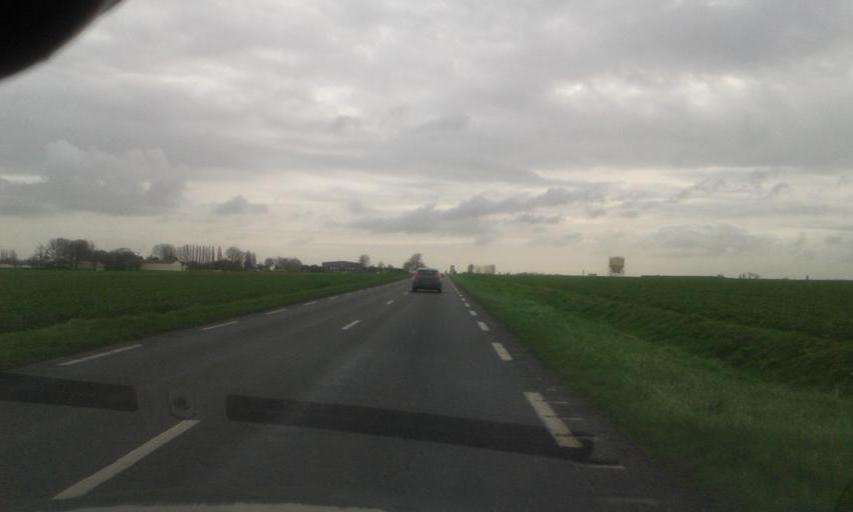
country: FR
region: Haute-Normandie
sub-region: Departement de la Seine-Maritime
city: Montmain
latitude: 49.3857
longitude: 1.2449
